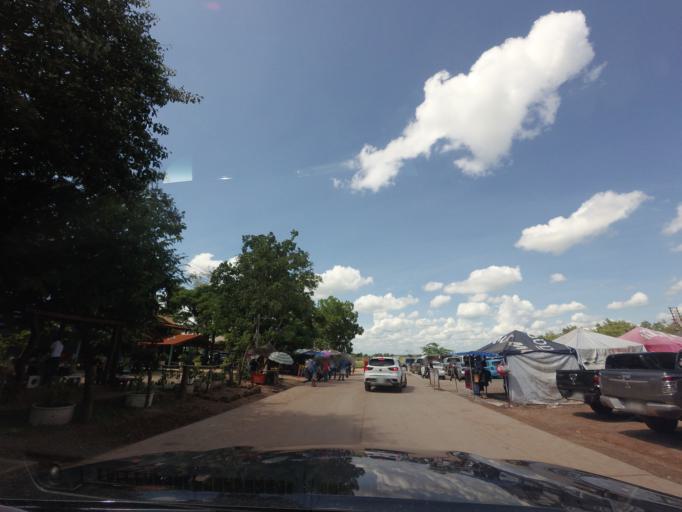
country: TH
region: Changwat Udon Thani
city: Ban Dung
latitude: 17.7441
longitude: 103.3583
